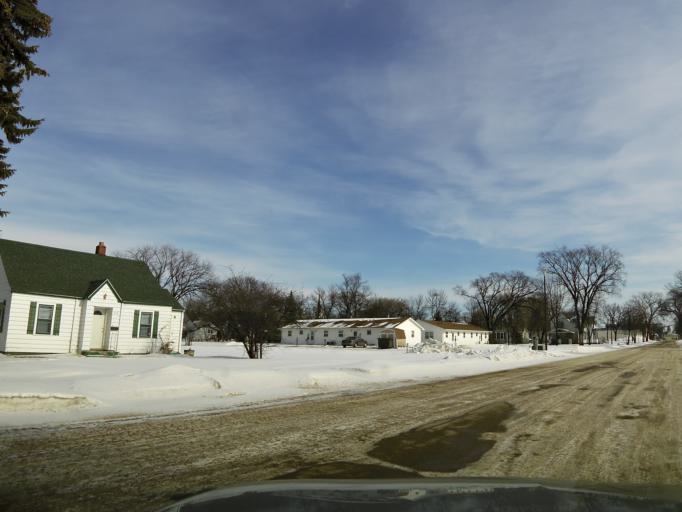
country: US
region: North Dakota
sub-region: Walsh County
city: Grafton
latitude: 48.4176
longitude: -97.4172
